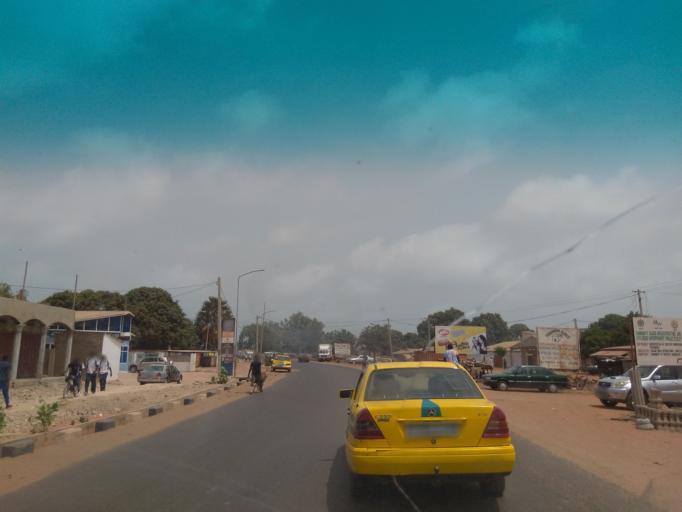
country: GM
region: Western
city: Sukuta
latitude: 13.4364
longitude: -16.6933
